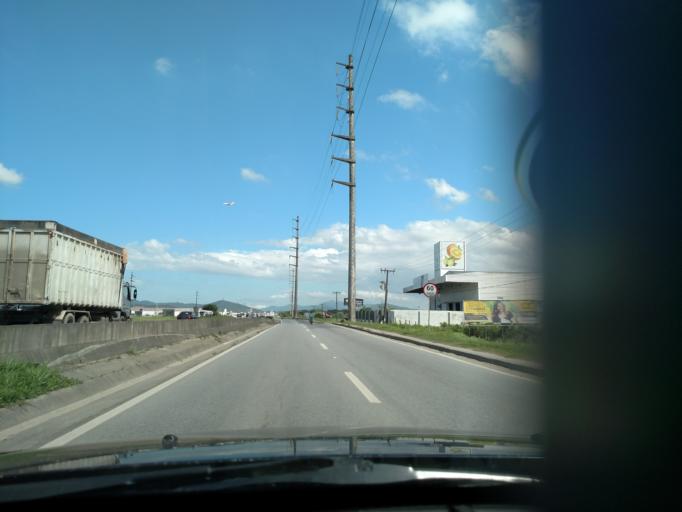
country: BR
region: Santa Catarina
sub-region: Itajai
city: Itajai
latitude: -26.9019
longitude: -48.7168
